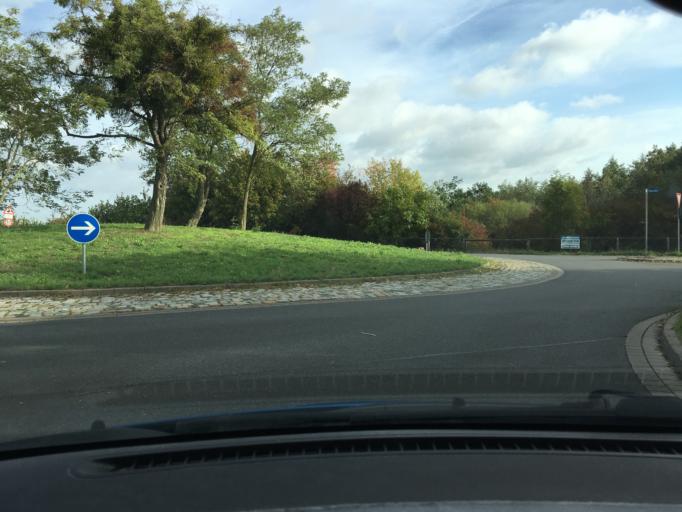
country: DE
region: Lower Saxony
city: Bad Nenndorf
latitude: 52.3376
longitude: 9.4042
